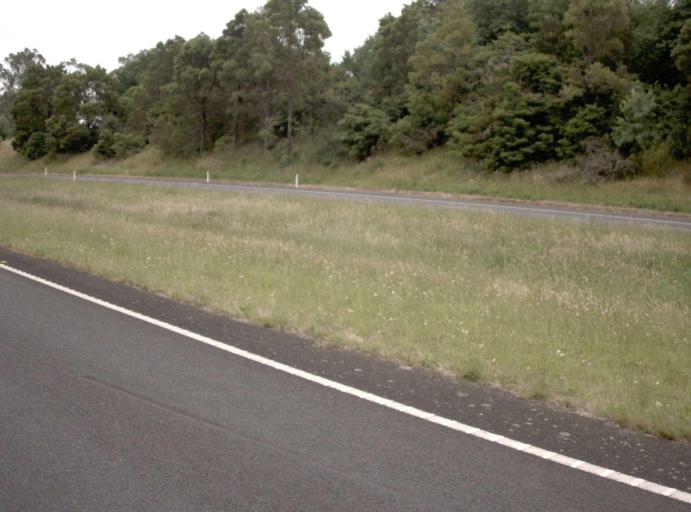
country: AU
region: Victoria
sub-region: Baw Baw
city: Warragul
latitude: -38.1183
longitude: 145.8664
